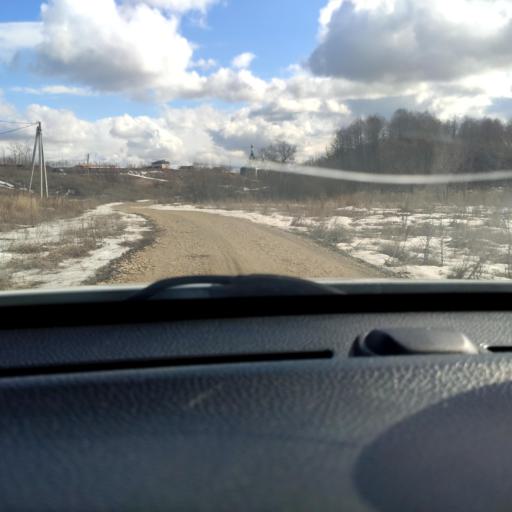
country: RU
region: Voronezj
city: Novaya Usman'
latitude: 51.6848
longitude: 39.3905
